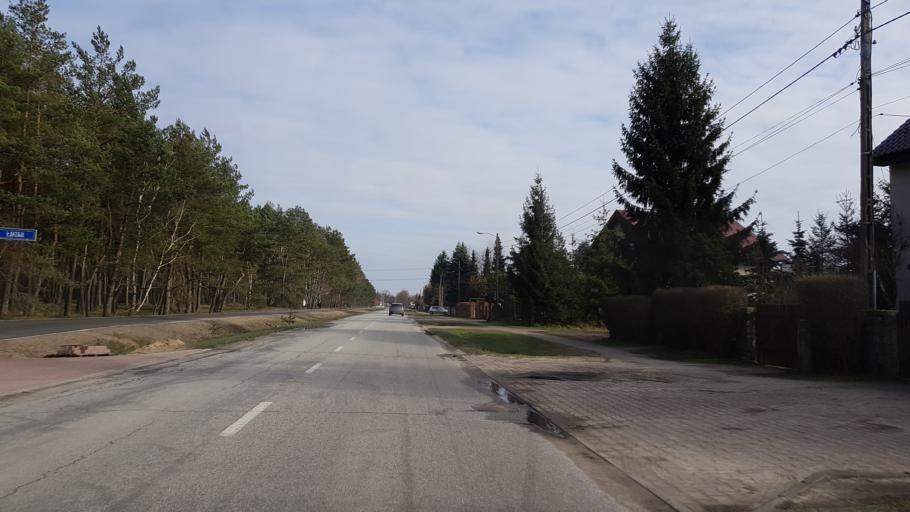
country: PL
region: West Pomeranian Voivodeship
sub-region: Powiat policki
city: Dobra
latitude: 53.4783
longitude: 14.4278
